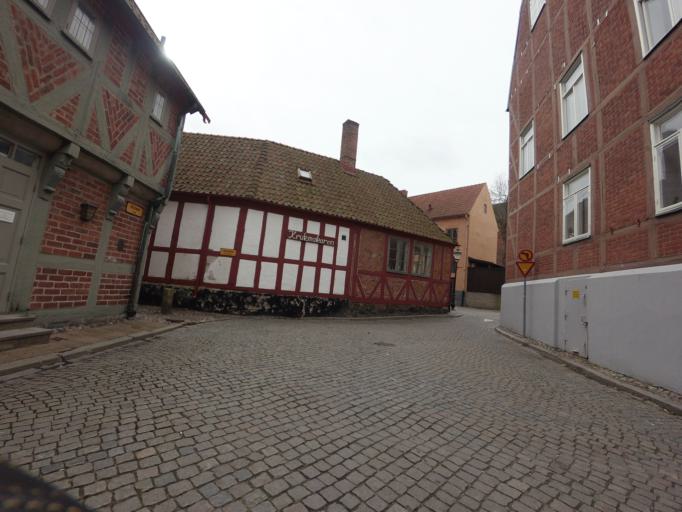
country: SE
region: Skane
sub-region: Ystads Kommun
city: Ystad
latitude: 55.4302
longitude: 13.8202
